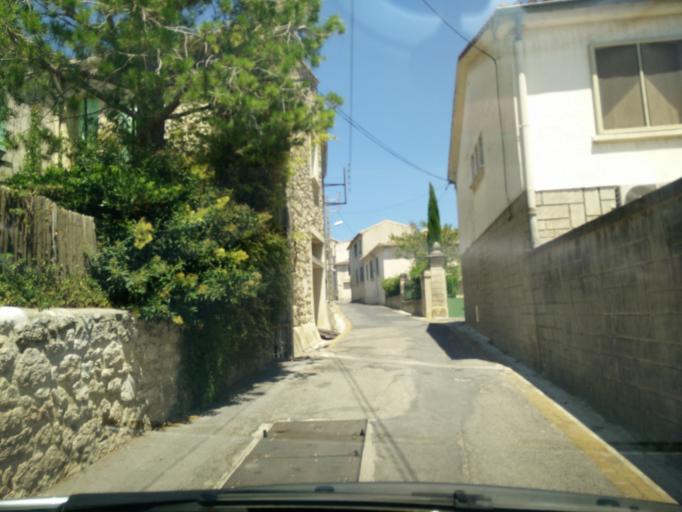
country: FR
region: Languedoc-Roussillon
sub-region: Departement de l'Herault
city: Saint-Christol
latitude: 43.7250
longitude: 4.0776
